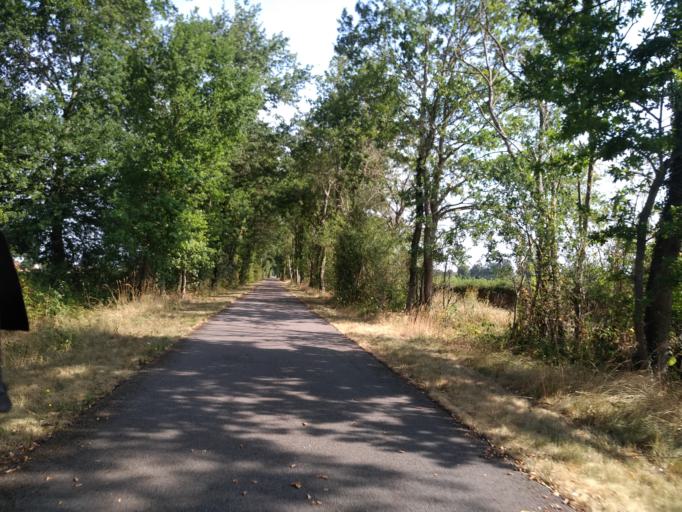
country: FR
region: Bourgogne
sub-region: Departement de Saone-et-Loire
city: Marcigny
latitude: 46.3176
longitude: 4.0285
